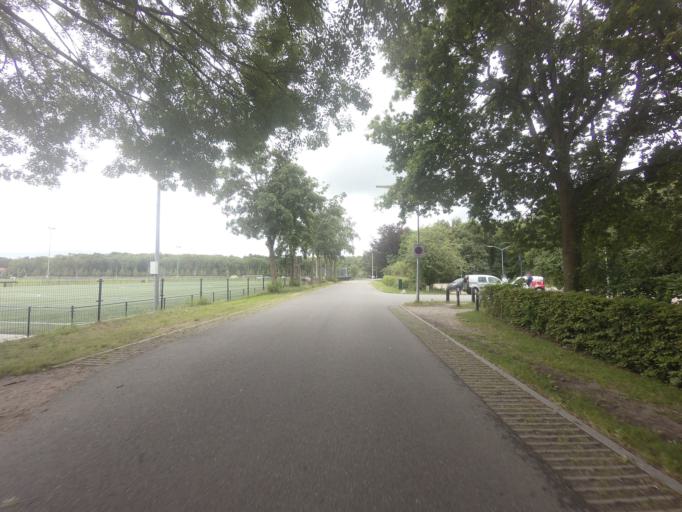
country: NL
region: North Holland
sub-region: Gemeente Bloemendaal
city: Bloemendaal
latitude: 52.4152
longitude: 4.6139
